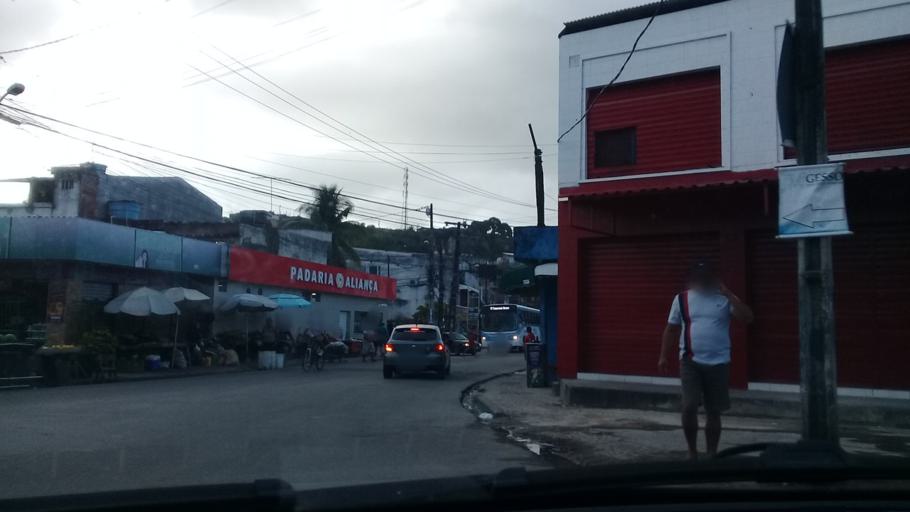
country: BR
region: Pernambuco
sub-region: Jaboatao Dos Guararapes
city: Jaboatao dos Guararapes
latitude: -8.1331
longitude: -34.9486
